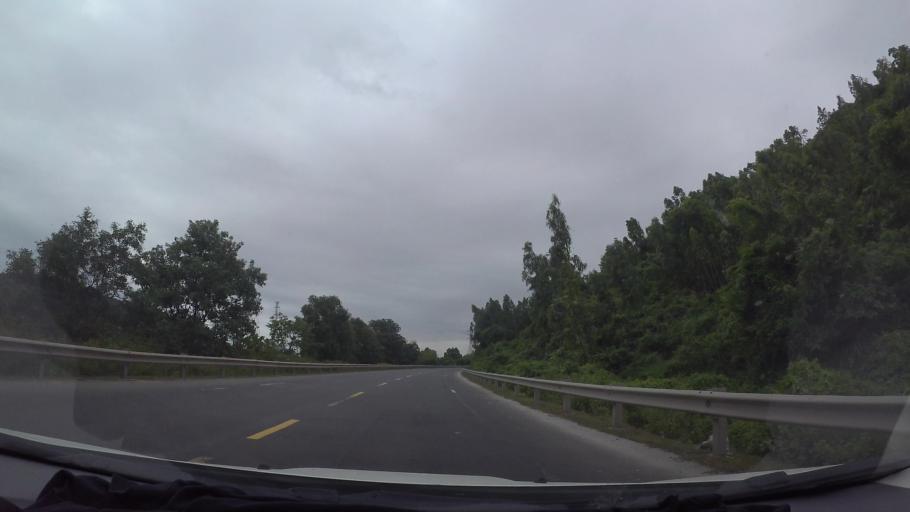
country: VN
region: Da Nang
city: Lien Chieu
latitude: 16.1196
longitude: 108.1028
